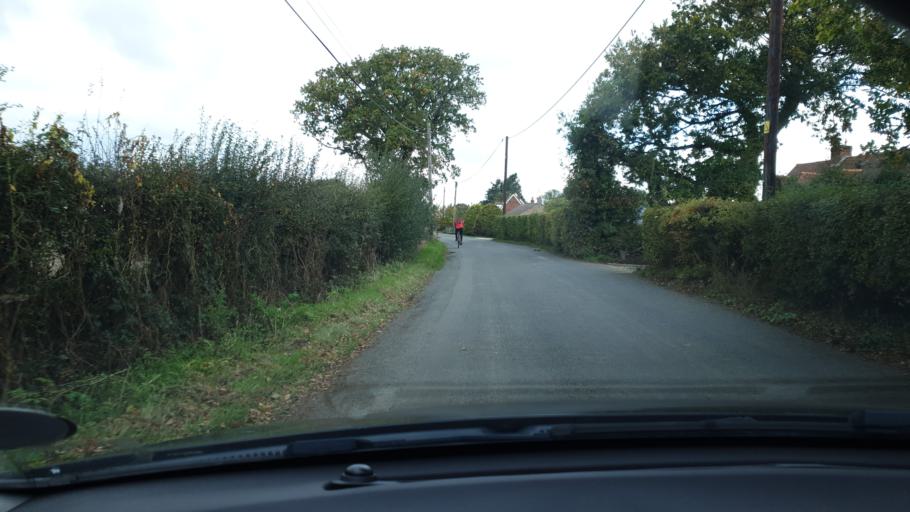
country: GB
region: England
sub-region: Essex
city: Mistley
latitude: 51.9308
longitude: 1.1016
